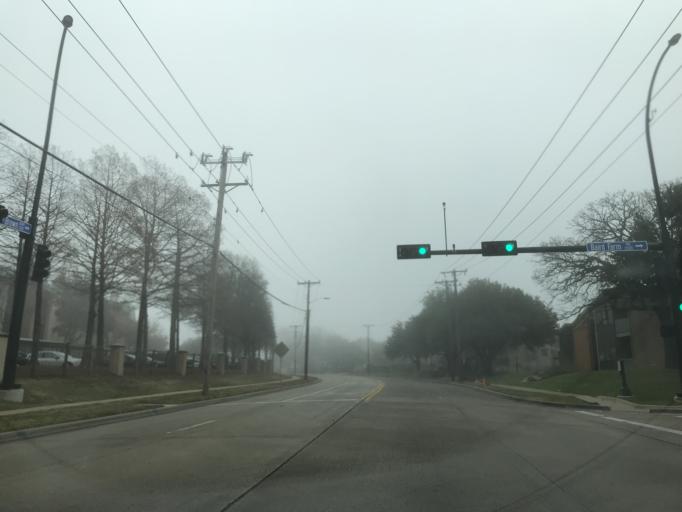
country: US
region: Texas
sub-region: Tarrant County
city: Arlington
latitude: 32.7731
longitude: -97.0854
